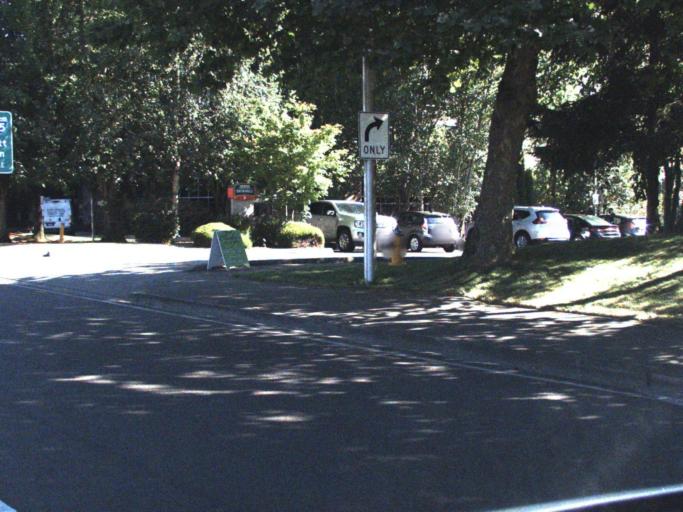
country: US
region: Washington
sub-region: King County
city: Tukwila
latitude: 47.4594
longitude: -122.2445
